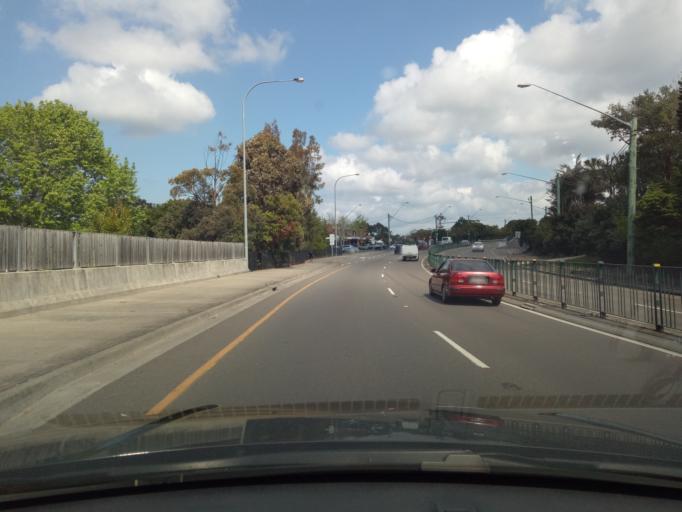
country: AU
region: New South Wales
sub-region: Gosford Shire
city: Forresters Beach
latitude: -33.4178
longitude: 151.4472
